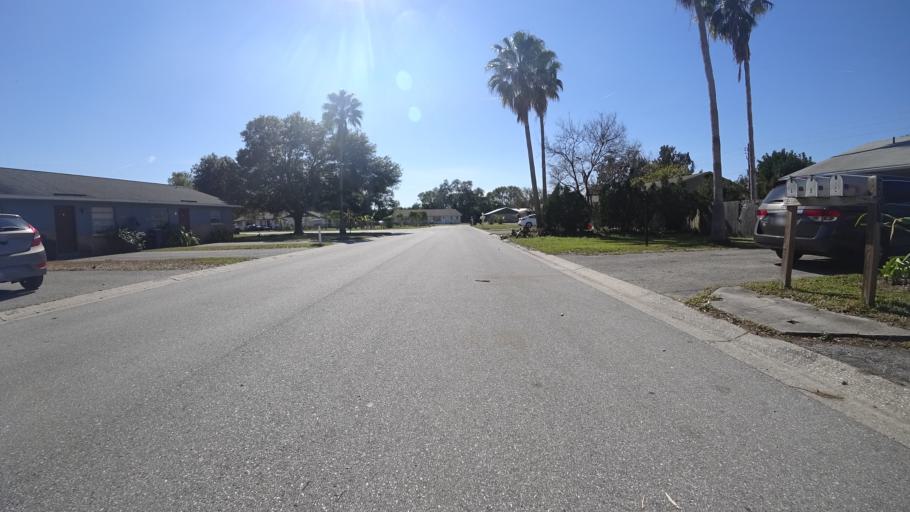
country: US
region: Florida
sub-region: Manatee County
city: West Bradenton
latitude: 27.4602
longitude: -82.6303
